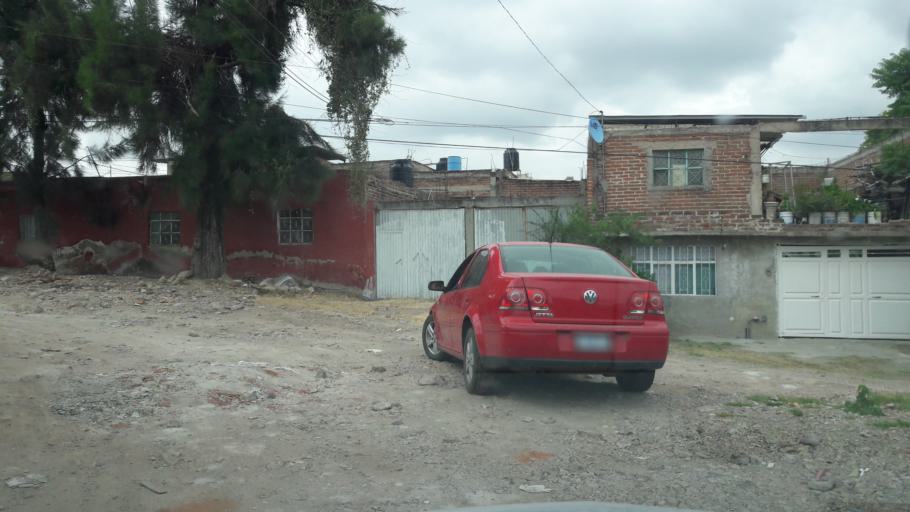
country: MX
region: Guanajuato
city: Leon
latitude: 21.1406
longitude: -101.7002
